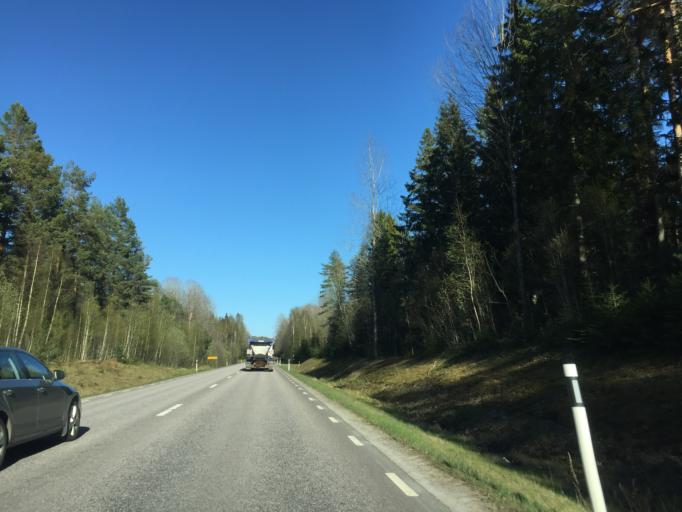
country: SE
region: OErebro
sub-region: Hallsbergs Kommun
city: Skollersta
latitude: 59.2523
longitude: 15.3551
